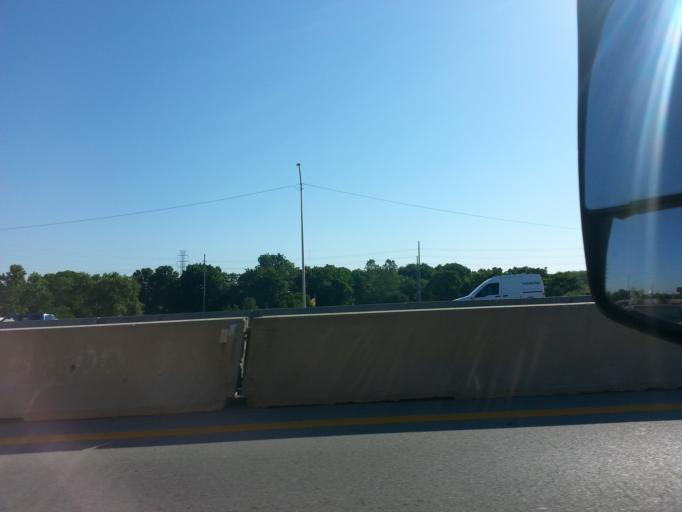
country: US
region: Indiana
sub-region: Clark County
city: Jeffersonville
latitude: 38.2592
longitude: -85.7240
